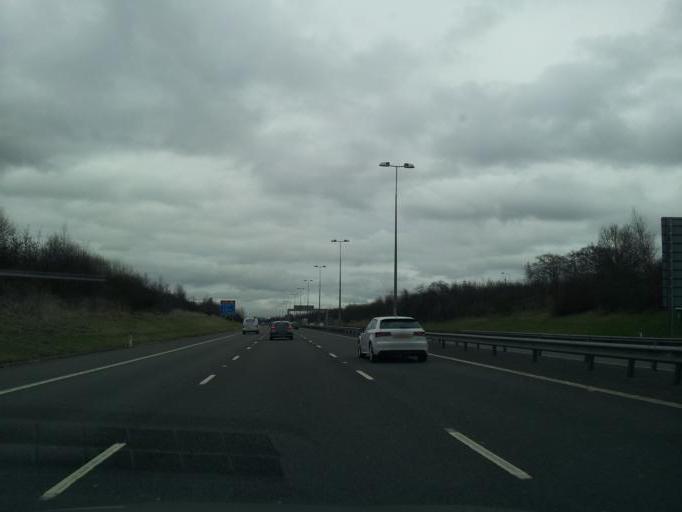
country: GB
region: England
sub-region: Staffordshire
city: Great Wyrley
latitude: 52.6654
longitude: -1.9911
